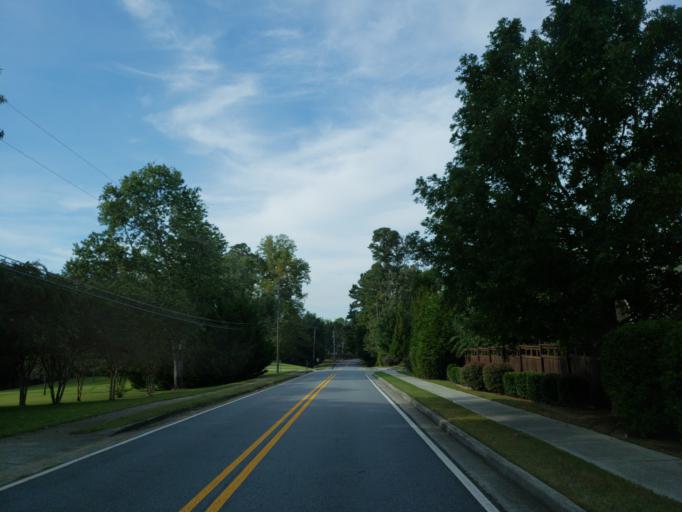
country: US
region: Georgia
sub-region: Cherokee County
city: Woodstock
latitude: 34.0518
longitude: -84.4968
